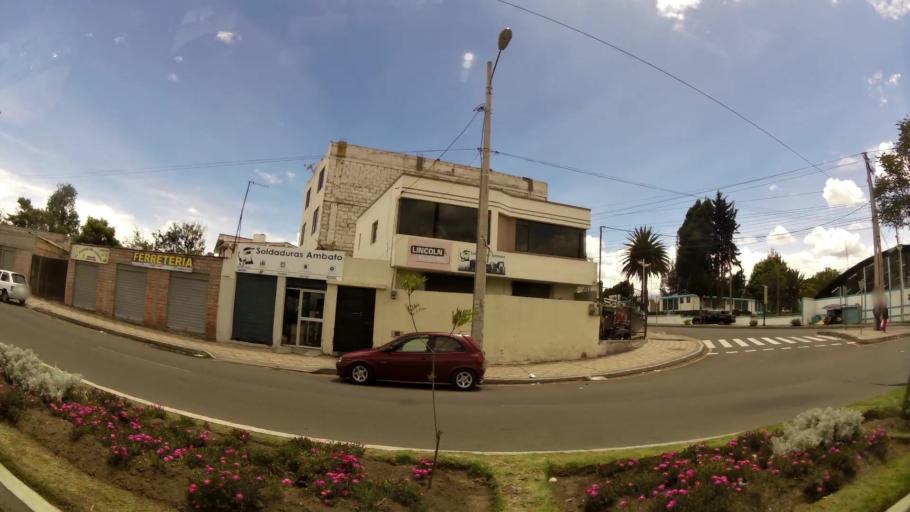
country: EC
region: Tungurahua
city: Ambato
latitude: -1.2583
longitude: -78.6139
